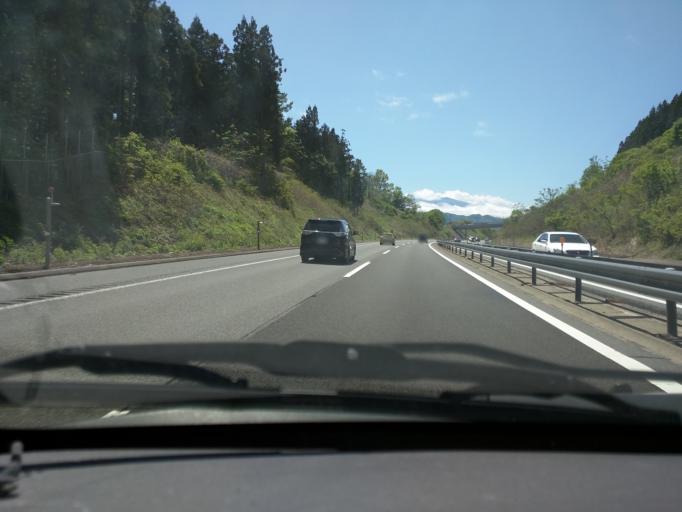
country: JP
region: Nagano
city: Nakano
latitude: 36.7774
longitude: 138.3181
